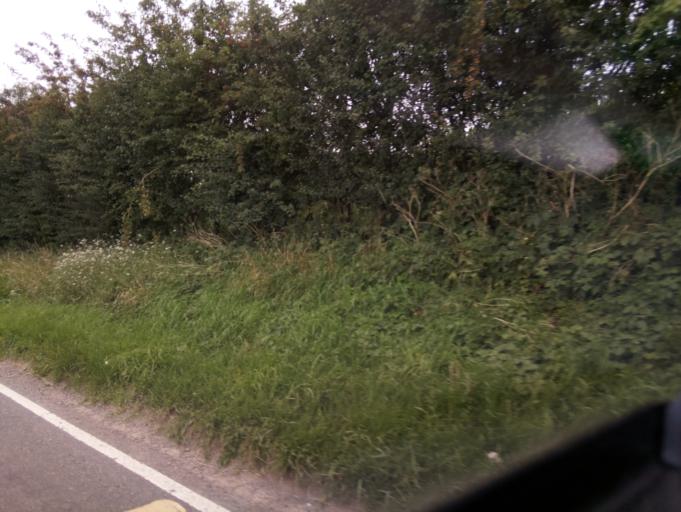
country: GB
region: England
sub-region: Somerset
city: Bradley Cross
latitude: 51.2597
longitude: -2.7555
